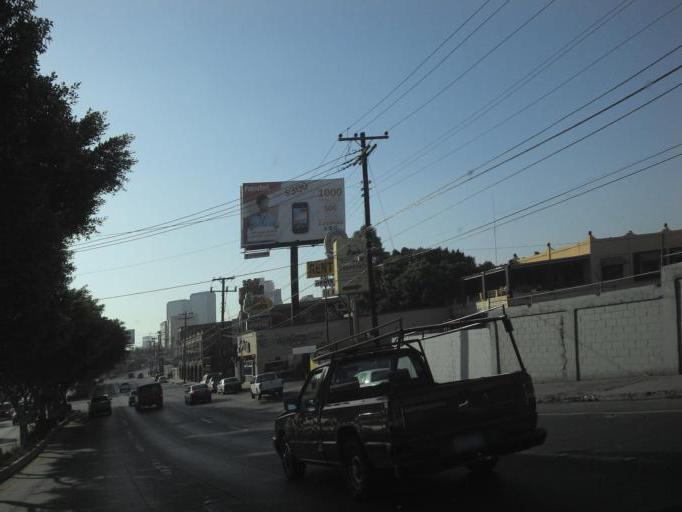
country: MX
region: Baja California
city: Tijuana
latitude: 32.5179
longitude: -117.0159
